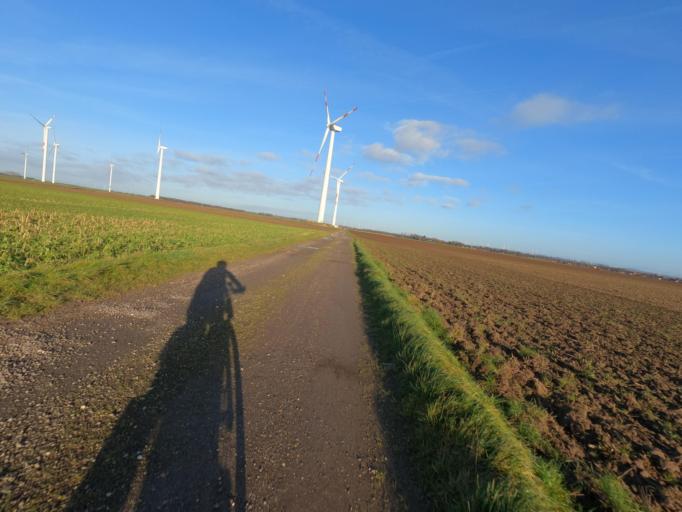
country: DE
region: North Rhine-Westphalia
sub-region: Regierungsbezirk Koln
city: Bedburg
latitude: 50.9726
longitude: 6.5002
